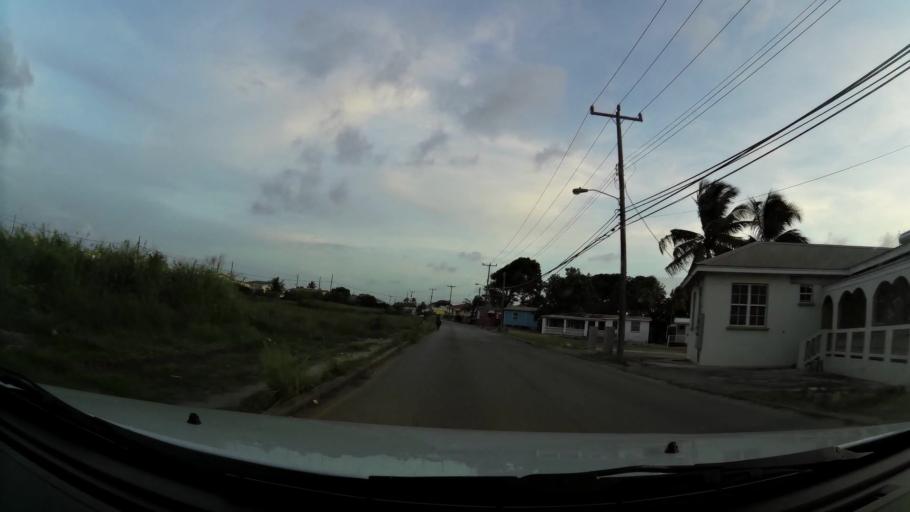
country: BB
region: Saint Philip
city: Crane
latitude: 13.1156
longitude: -59.4756
